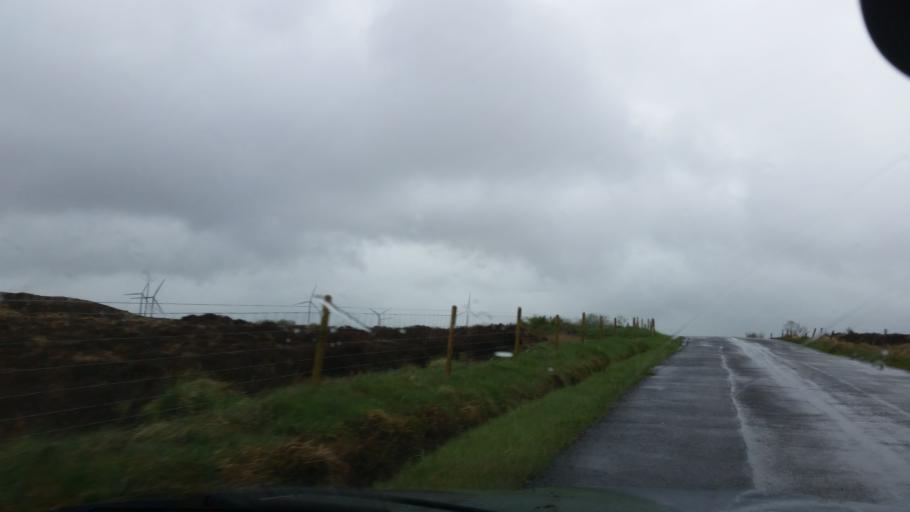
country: GB
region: Northern Ireland
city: Fivemiletown
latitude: 54.4353
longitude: -7.3271
